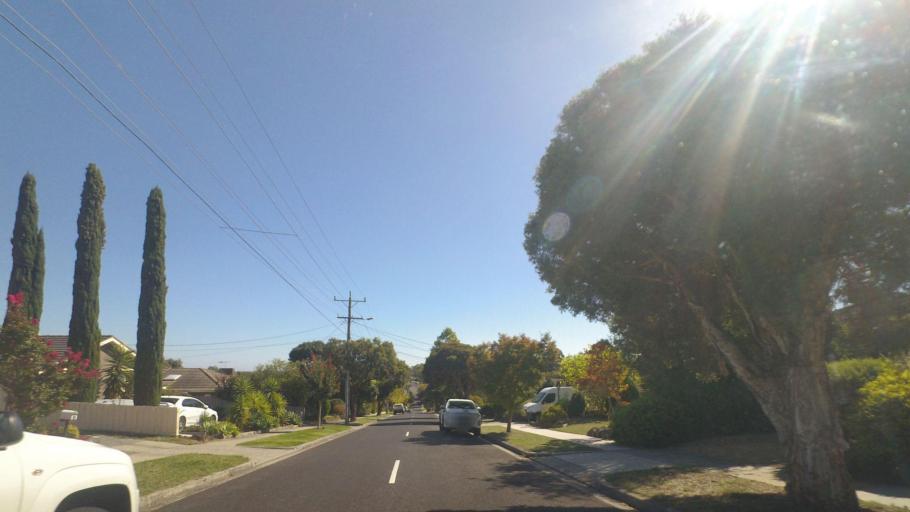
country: AU
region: Victoria
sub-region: Manningham
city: Donvale
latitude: -37.8002
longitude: 145.1722
